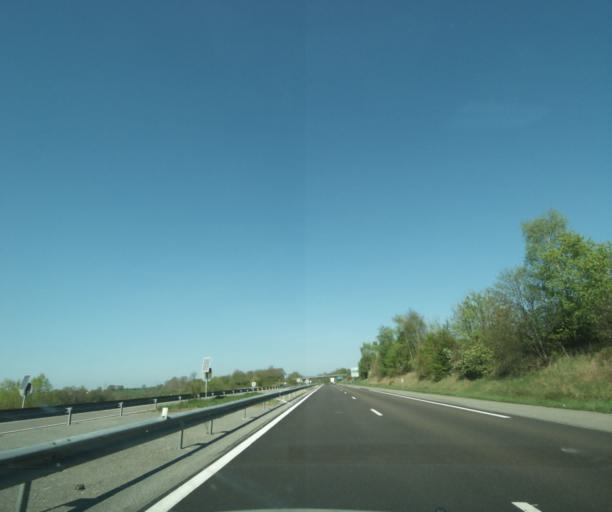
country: FR
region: Bourgogne
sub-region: Departement de la Nievre
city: Cosne-Cours-sur-Loire
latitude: 47.4402
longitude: 2.9428
